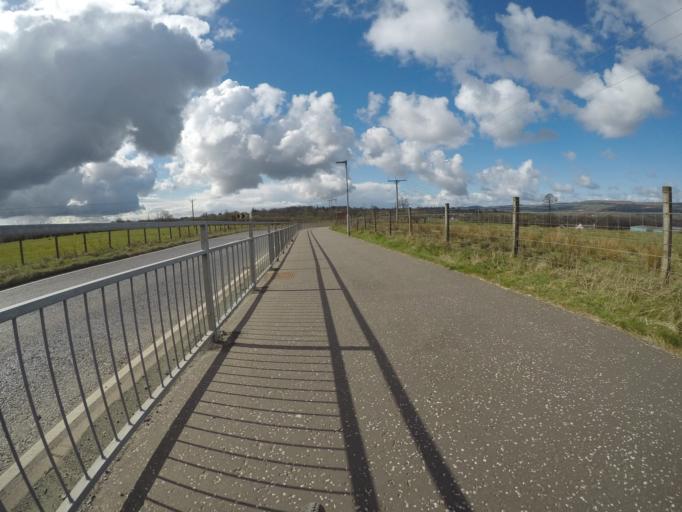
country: GB
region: Scotland
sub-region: North Ayrshire
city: Beith
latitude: 55.7402
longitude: -4.6544
